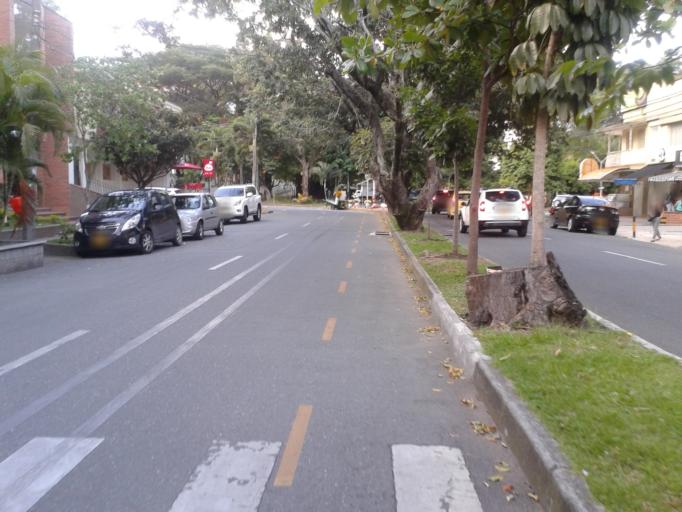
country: CO
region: Antioquia
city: Medellin
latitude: 6.2440
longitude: -75.5970
